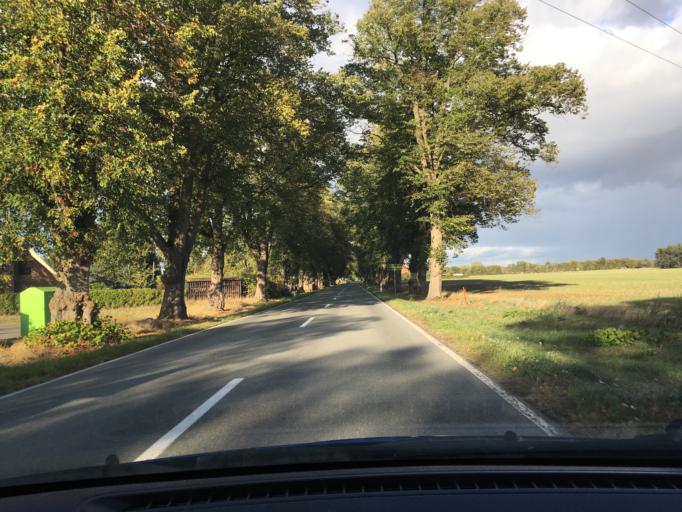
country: DE
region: Mecklenburg-Vorpommern
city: Boizenburg
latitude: 53.4003
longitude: 10.8206
